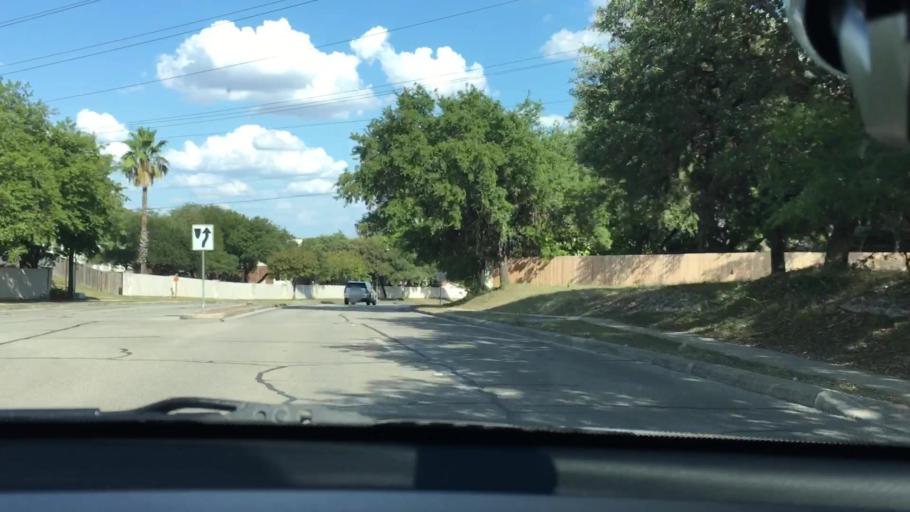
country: US
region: Texas
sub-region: Bexar County
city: Selma
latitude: 29.5675
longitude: -98.3152
